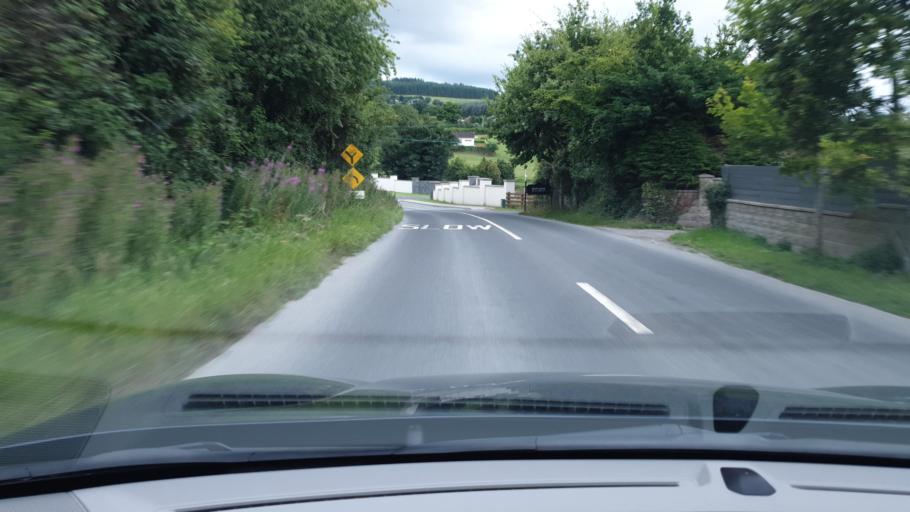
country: IE
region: Leinster
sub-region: South Dublin
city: Saggart
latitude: 53.2763
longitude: -6.4498
